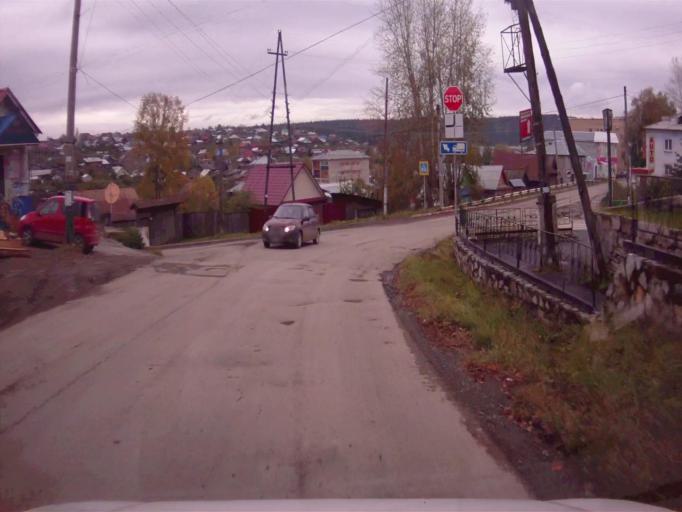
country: RU
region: Chelyabinsk
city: Nyazepetrovsk
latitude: 56.0538
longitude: 59.6029
